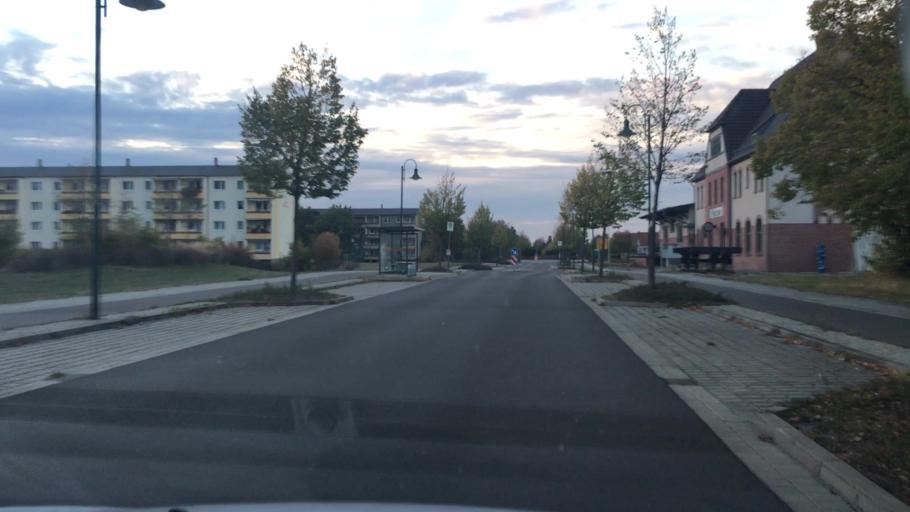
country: DE
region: Brandenburg
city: Welzow
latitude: 51.5793
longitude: 14.1699
